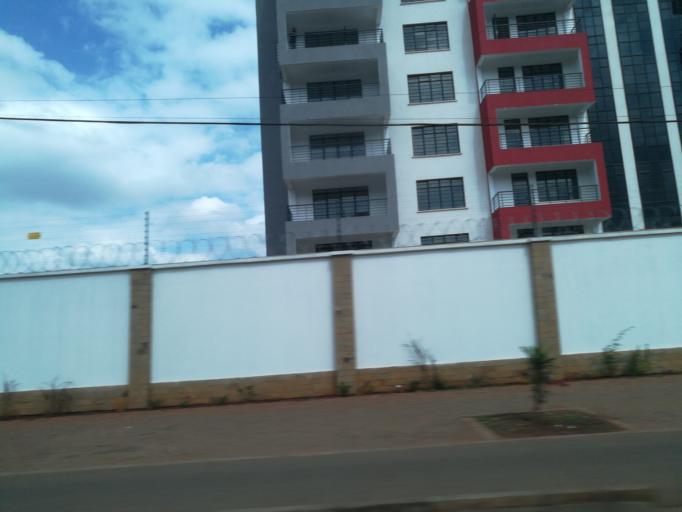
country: KE
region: Nairobi Area
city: Nairobi
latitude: -1.2818
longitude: 36.7880
